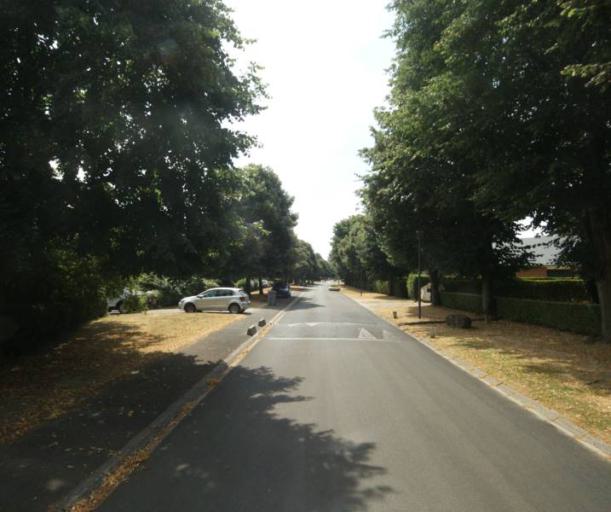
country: FR
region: Nord-Pas-de-Calais
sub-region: Departement du Nord
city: Mouvaux
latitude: 50.7231
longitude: 3.1227
